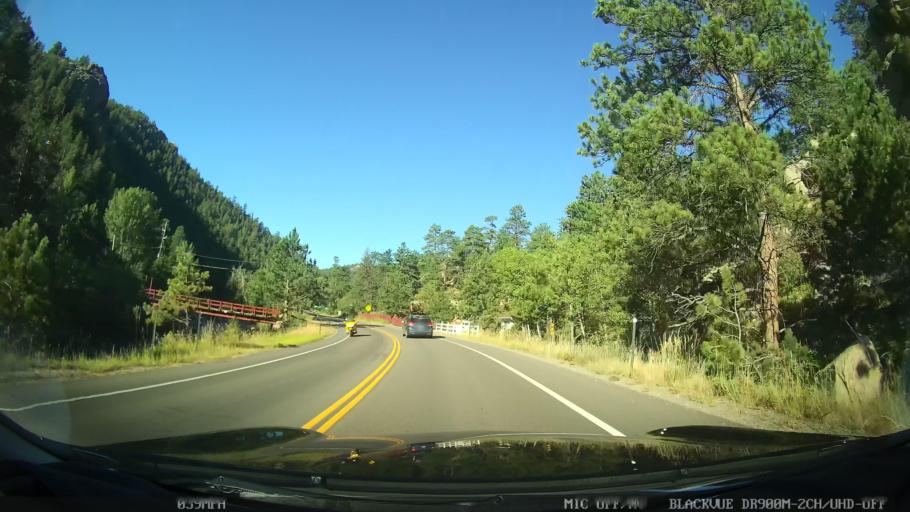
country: US
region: Colorado
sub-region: Larimer County
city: Estes Park
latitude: 40.3914
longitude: -105.4598
